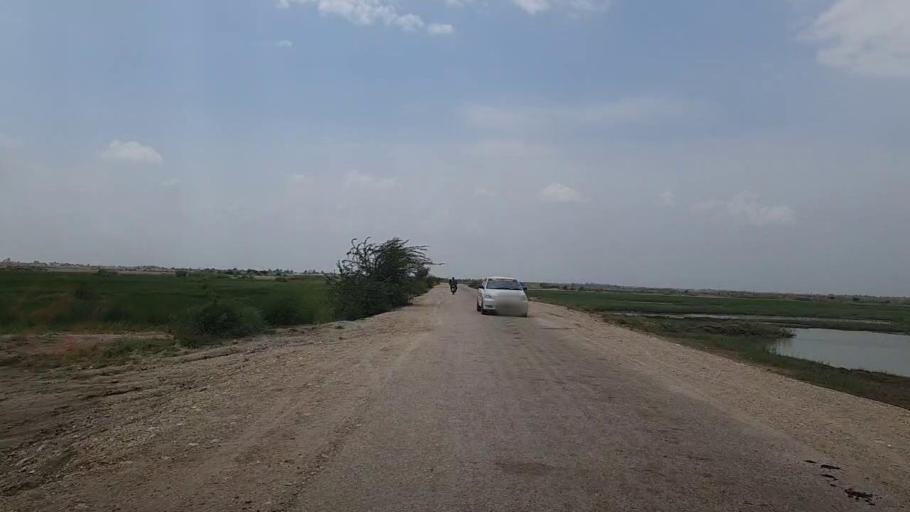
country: PK
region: Sindh
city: Kandhkot
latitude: 28.2950
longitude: 69.1397
